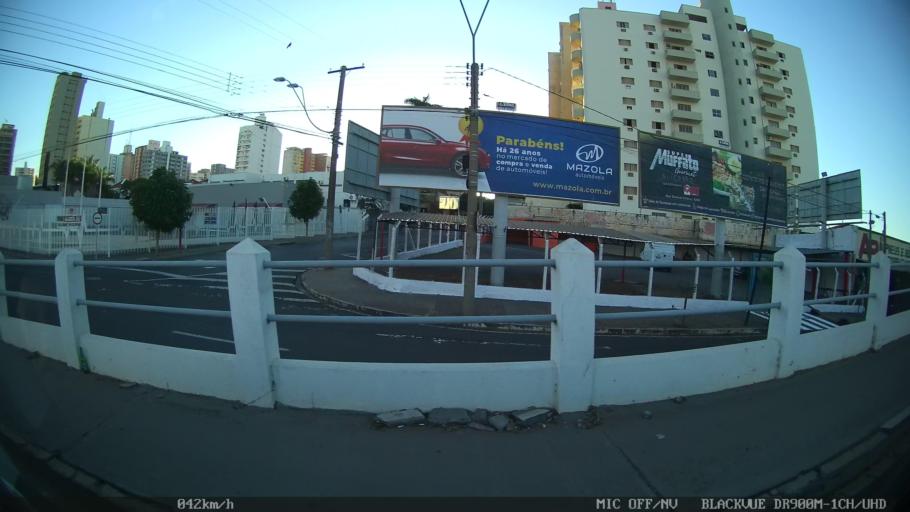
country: BR
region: Sao Paulo
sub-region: Sao Jose Do Rio Preto
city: Sao Jose do Rio Preto
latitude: -20.8116
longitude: -49.3758
